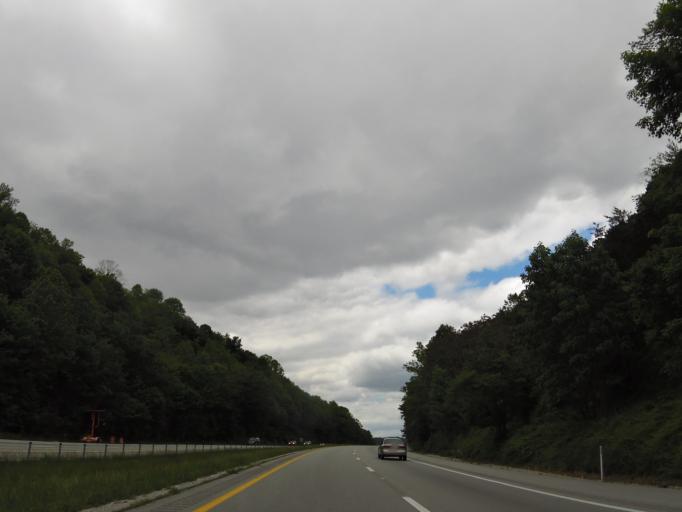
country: US
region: Kentucky
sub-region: Rockcastle County
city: Mount Vernon
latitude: 37.3266
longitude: -84.3025
